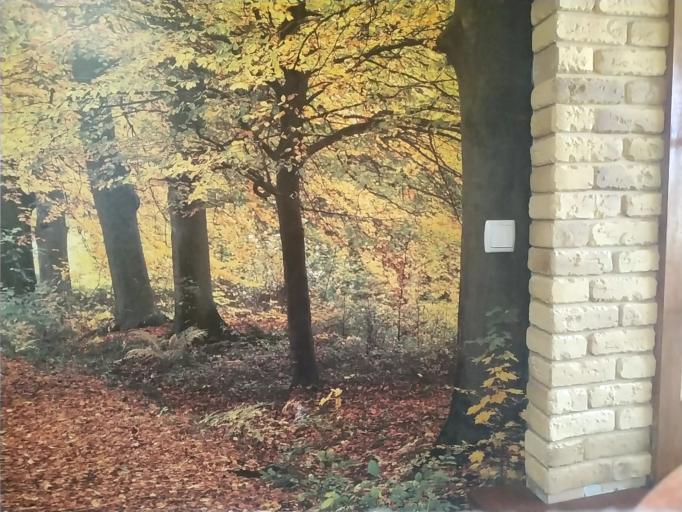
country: RU
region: Tverskaya
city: Vyshniy Volochek
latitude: 57.6601
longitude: 34.5410
